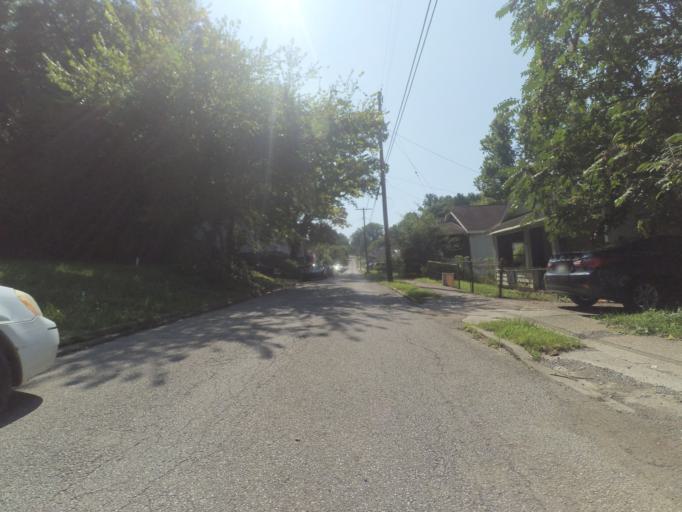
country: US
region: West Virginia
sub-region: Cabell County
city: Huntington
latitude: 38.4136
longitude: -82.4088
